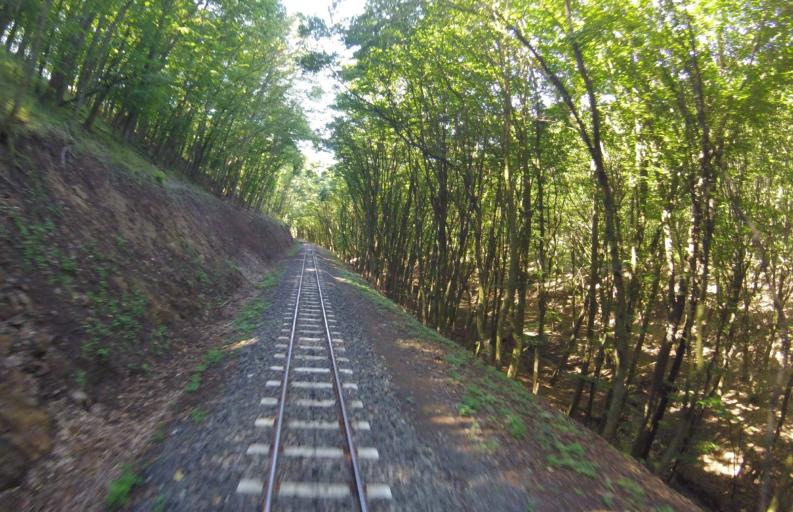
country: HU
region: Pest
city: Szob
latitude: 47.8868
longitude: 18.8679
